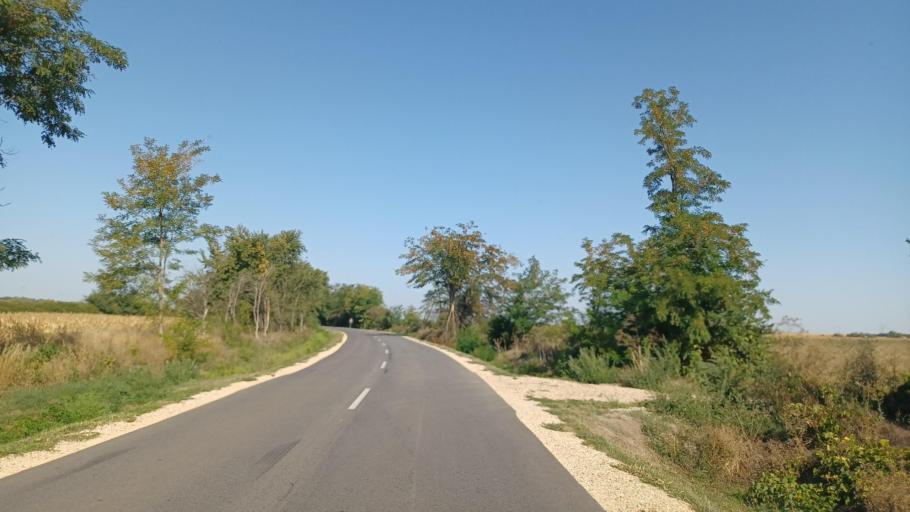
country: HU
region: Tolna
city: Nemetker
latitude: 46.6956
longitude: 18.7947
